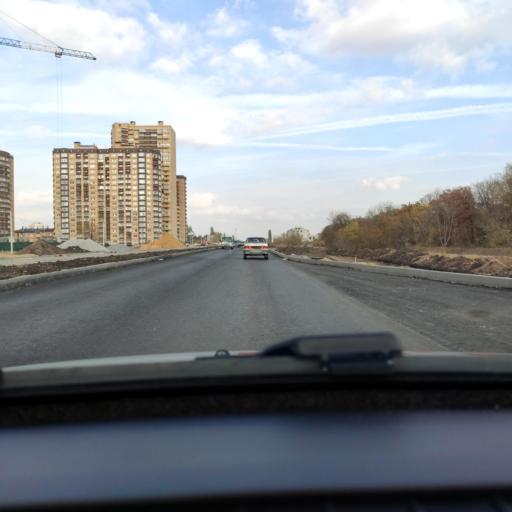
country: RU
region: Voronezj
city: Shilovo
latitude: 51.5649
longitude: 39.1220
